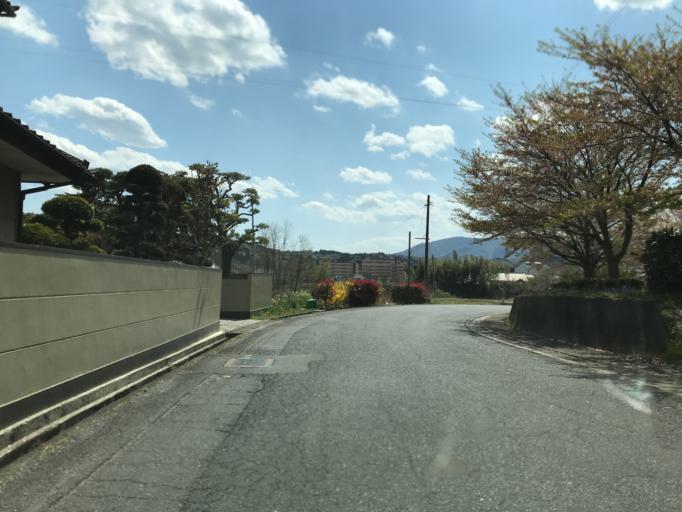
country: JP
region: Fukushima
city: Iwaki
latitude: 37.0719
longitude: 140.8446
